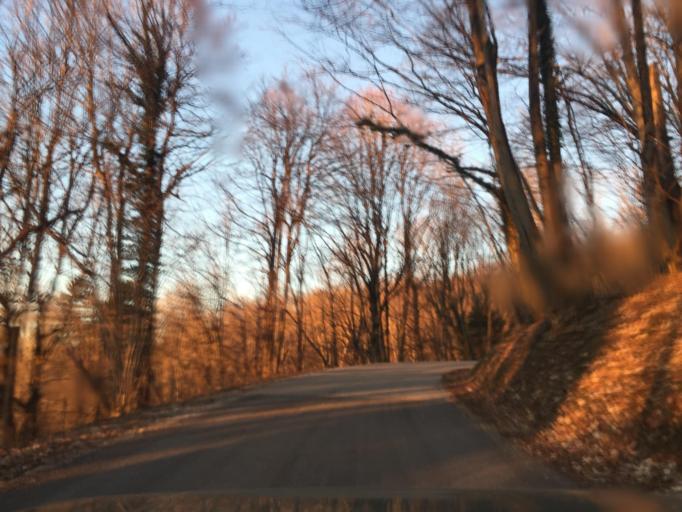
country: SI
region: Kanal
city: Kanal
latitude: 46.0736
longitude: 13.6519
